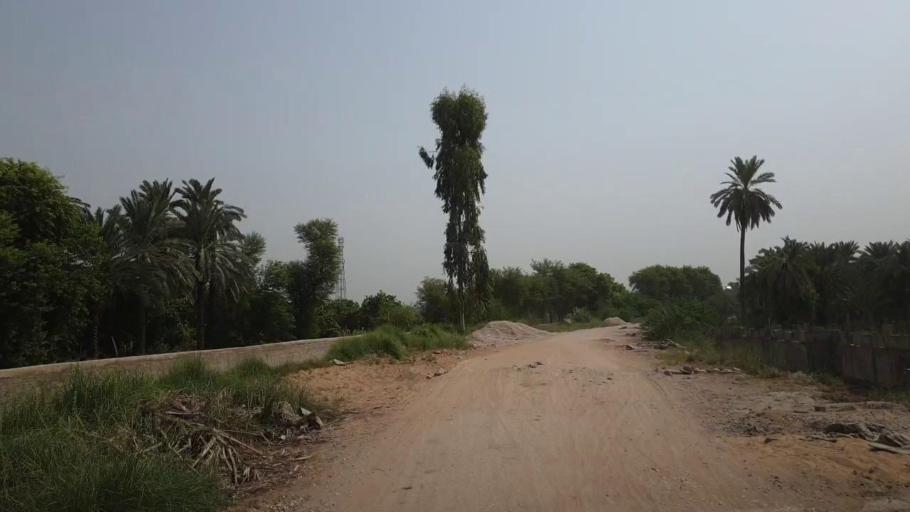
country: PK
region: Sindh
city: Gambat
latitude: 27.3813
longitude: 68.5132
